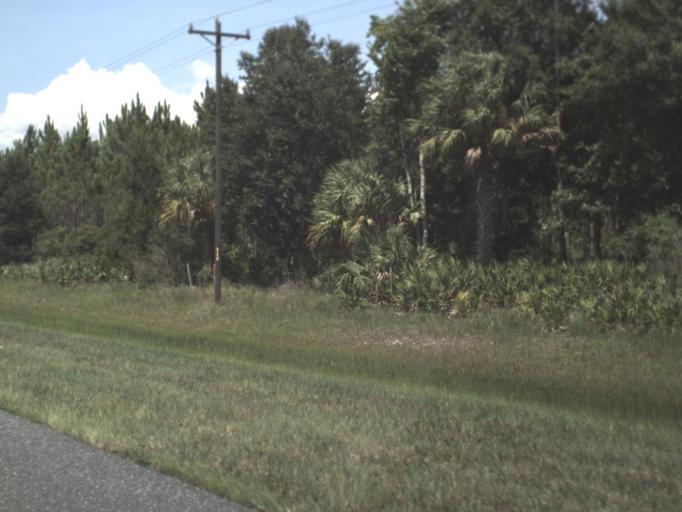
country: US
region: Florida
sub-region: Levy County
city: Inglis
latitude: 29.0837
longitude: -82.6393
